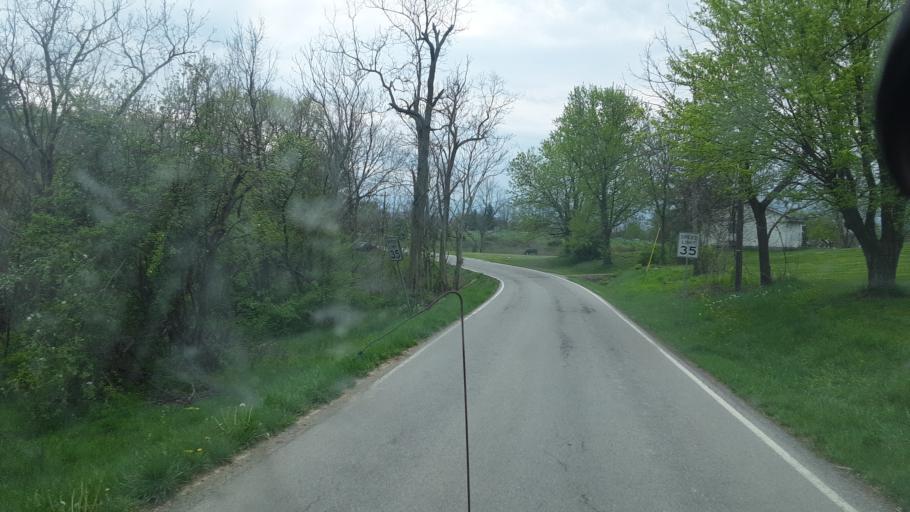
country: US
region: Kentucky
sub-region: Owen County
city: Owenton
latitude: 38.6446
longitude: -84.7747
